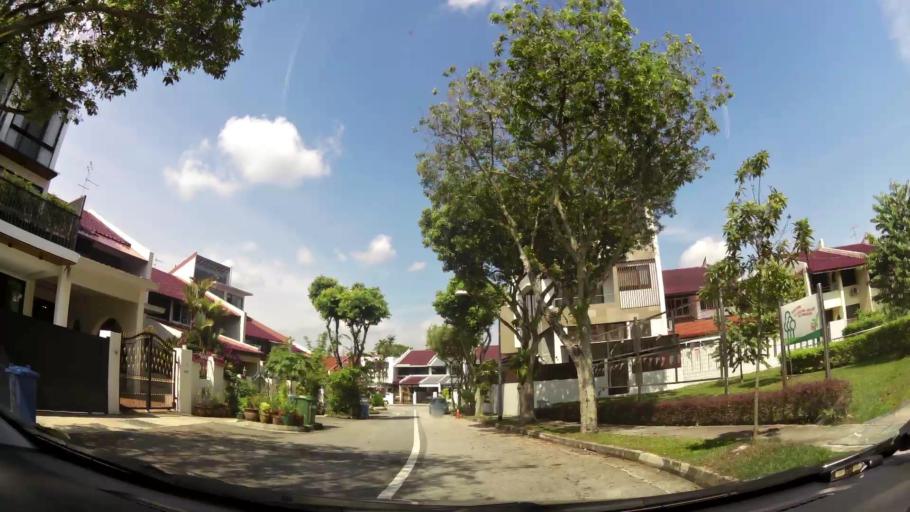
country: SG
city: Singapore
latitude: 1.3717
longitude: 103.8343
